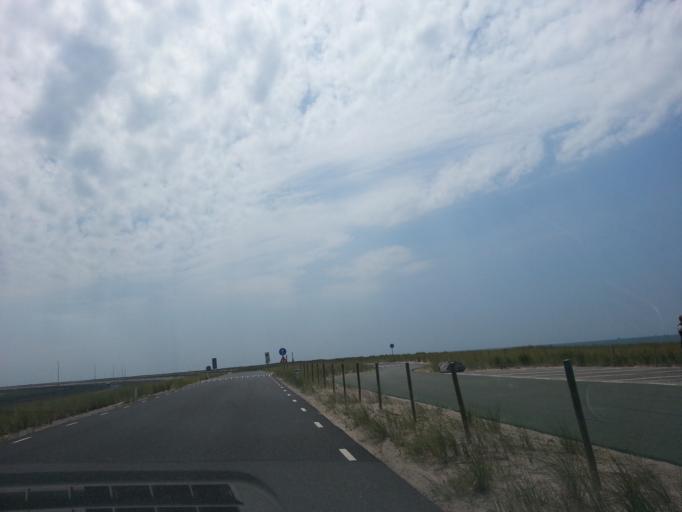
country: NL
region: South Holland
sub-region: Gemeente Goeree-Overflakkee
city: Goedereede
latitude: 51.9710
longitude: 3.9697
